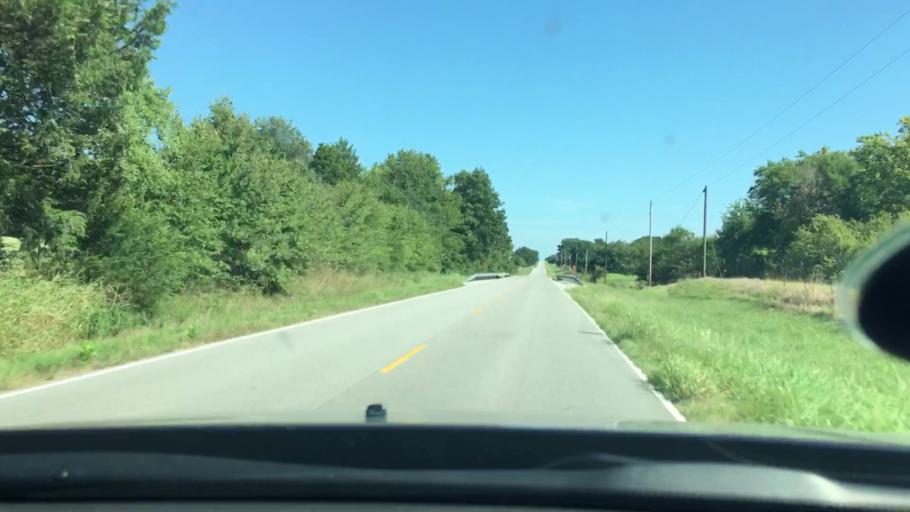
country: US
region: Oklahoma
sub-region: Johnston County
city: Tishomingo
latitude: 34.2874
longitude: -96.5487
